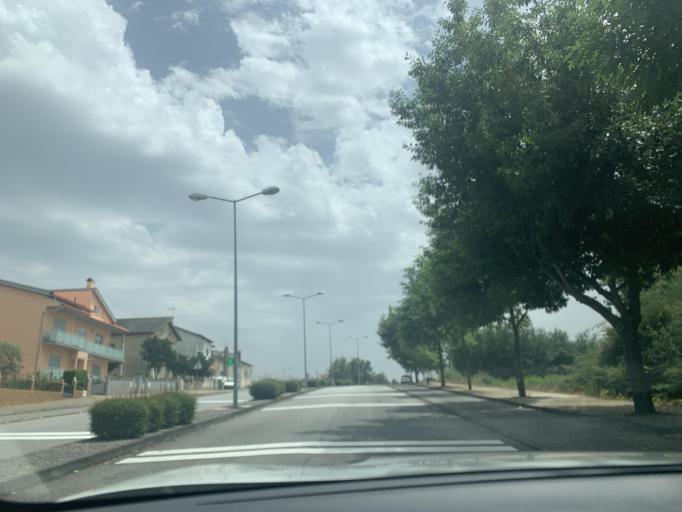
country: PT
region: Viseu
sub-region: Mangualde
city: Mangualde
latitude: 40.5964
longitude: -7.7580
